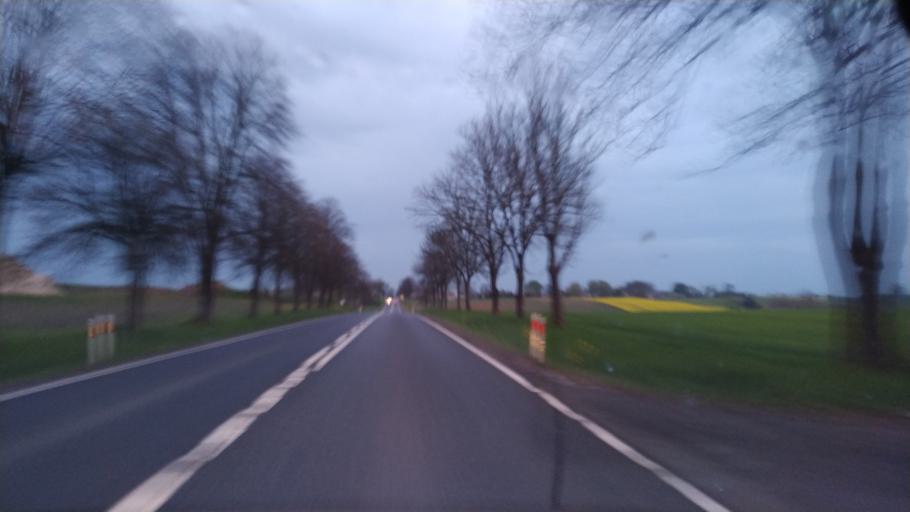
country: PL
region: West Pomeranian Voivodeship
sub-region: Powiat walecki
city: Walcz
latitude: 53.2470
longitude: 16.5426
